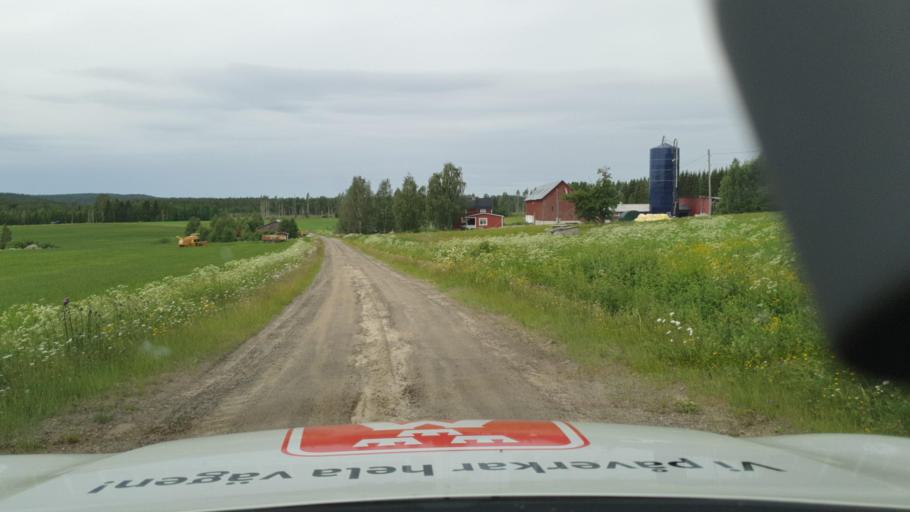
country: SE
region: Vaesterbotten
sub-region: Robertsfors Kommun
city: Robertsfors
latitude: 64.2851
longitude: 20.6669
